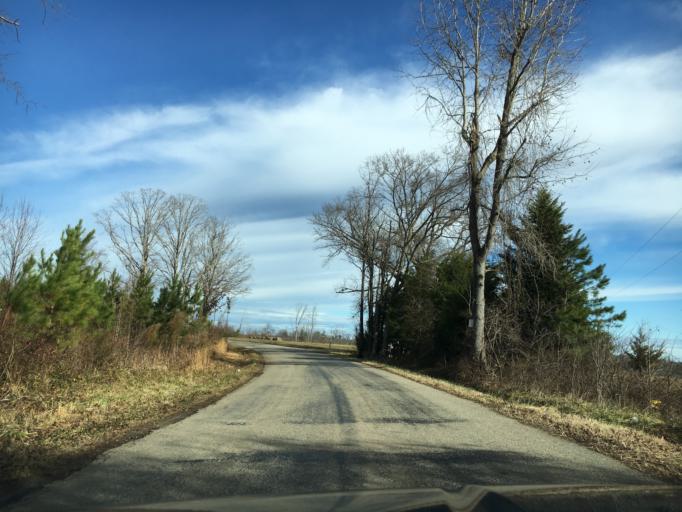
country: US
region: Virginia
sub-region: Nottoway County
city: Crewe
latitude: 37.2687
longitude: -78.2182
